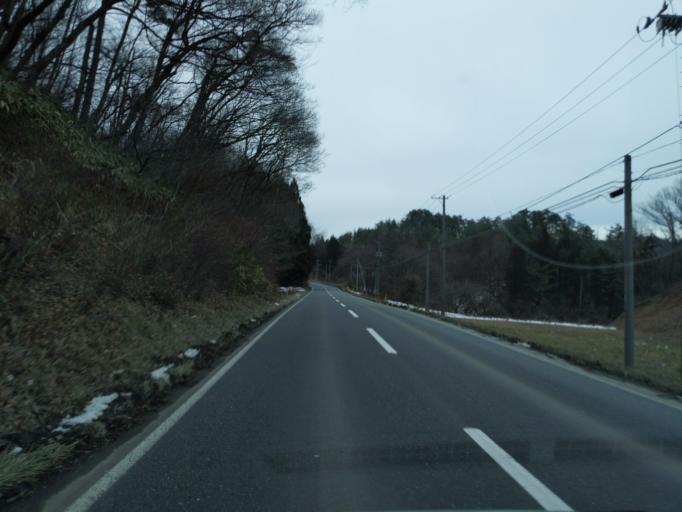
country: JP
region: Iwate
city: Mizusawa
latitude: 39.1453
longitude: 141.2446
